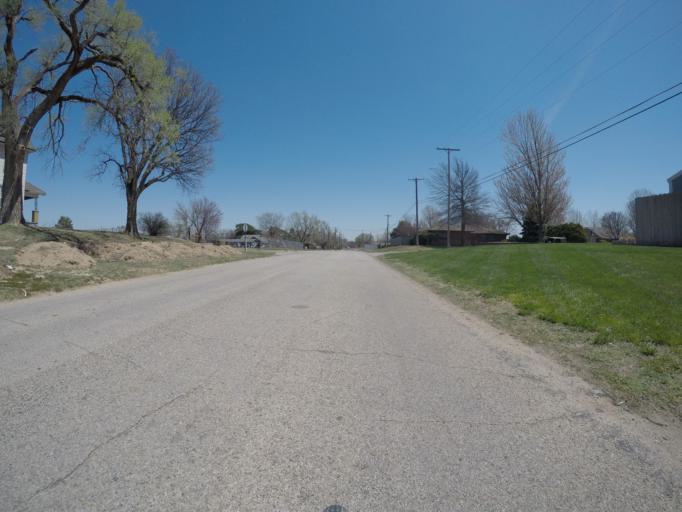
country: US
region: Kansas
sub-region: Pratt County
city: Pratt
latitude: 37.6421
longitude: -98.7547
